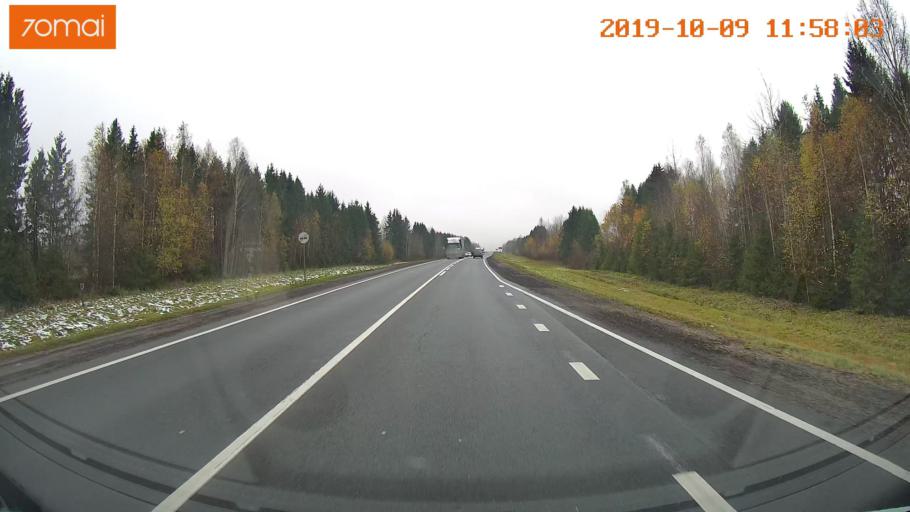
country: RU
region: Vologda
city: Gryazovets
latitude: 58.7236
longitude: 40.2959
